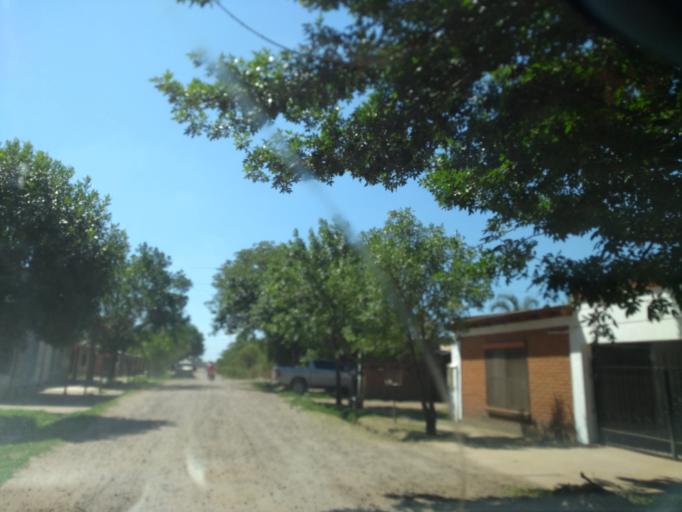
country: AR
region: Chaco
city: Fontana
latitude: -27.4123
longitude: -59.0359
